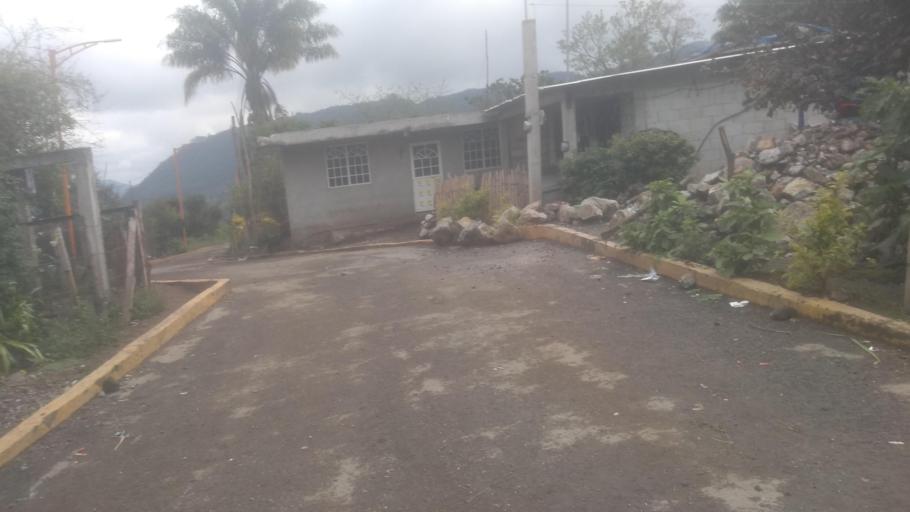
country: MX
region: Veracruz
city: Chocaman
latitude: 18.9869
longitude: -97.0568
